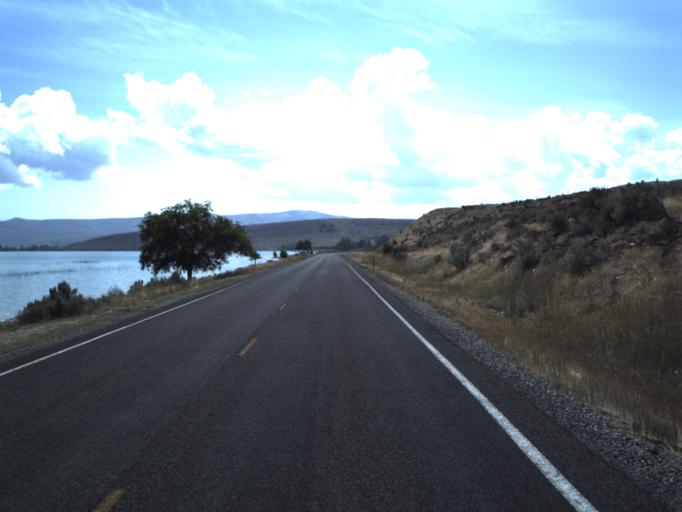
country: US
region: Utah
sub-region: Rich County
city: Randolph
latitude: 41.8694
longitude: -111.3653
